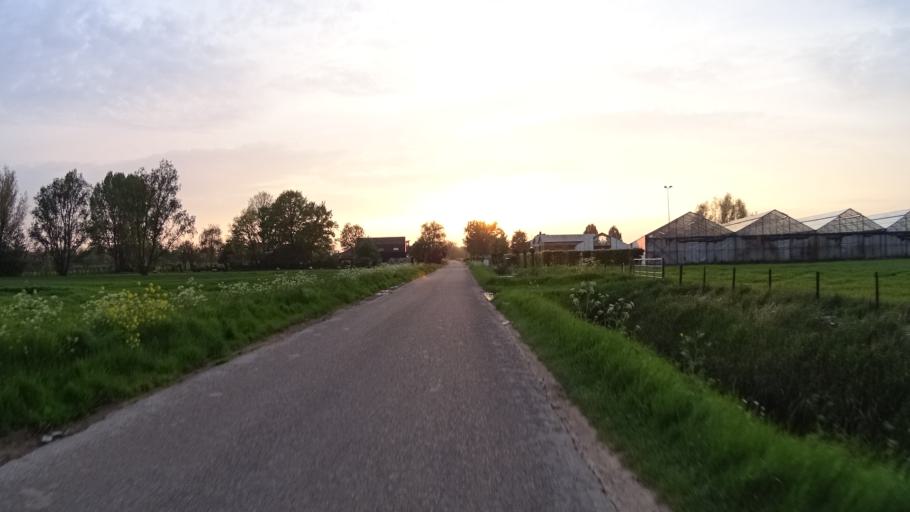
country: NL
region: North Brabant
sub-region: Gemeente Woudrichem
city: Woudrichem
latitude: 51.8118
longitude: 4.9883
